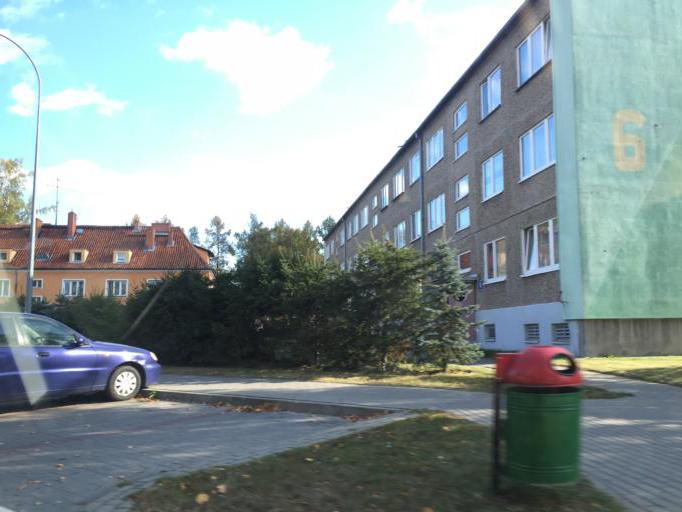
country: PL
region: Warmian-Masurian Voivodeship
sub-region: Powiat bartoszycki
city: Bartoszyce
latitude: 54.2465
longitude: 20.8091
